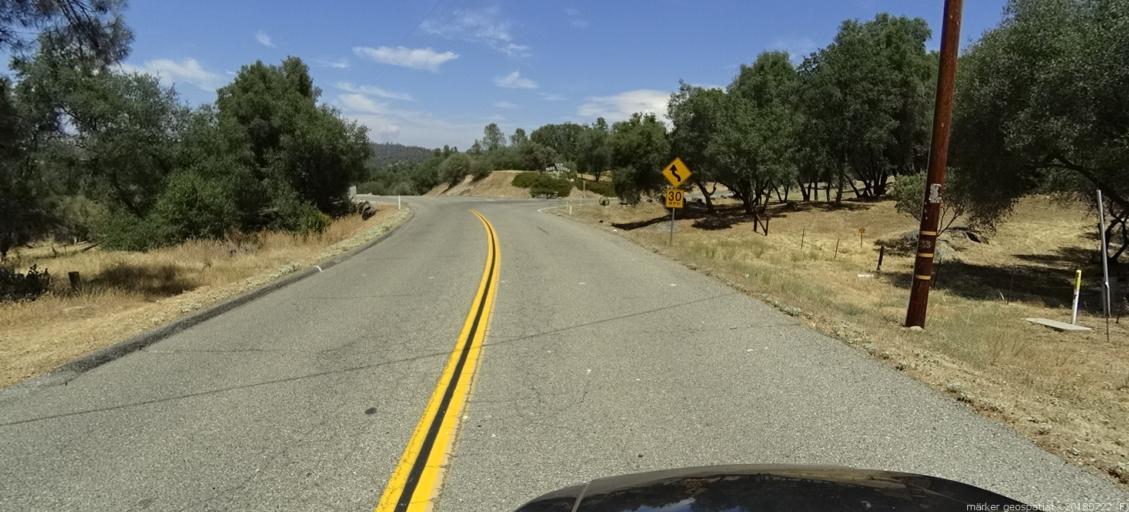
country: US
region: California
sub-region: Madera County
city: Yosemite Lakes
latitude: 37.2037
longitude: -119.7226
